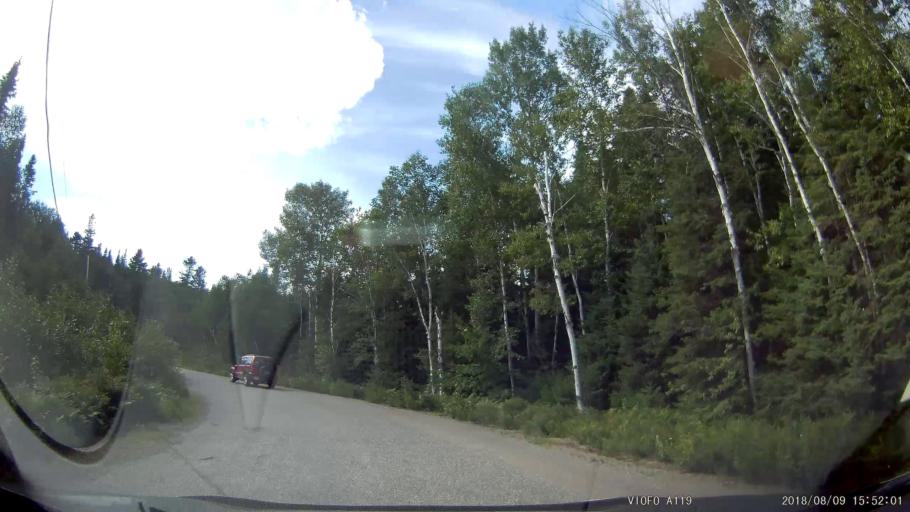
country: CA
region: Ontario
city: Rayside-Balfour
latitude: 46.5968
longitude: -81.5326
